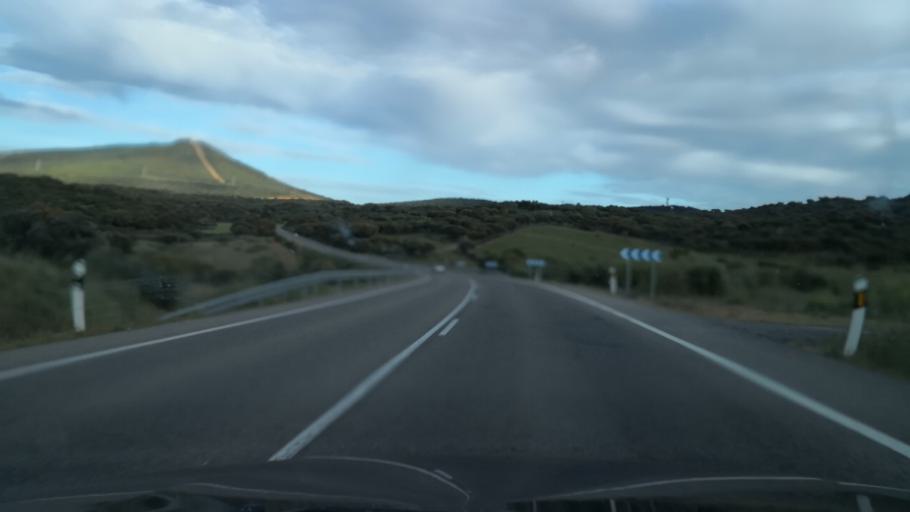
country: ES
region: Extremadura
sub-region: Provincia de Caceres
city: Pedroso de Acim
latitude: 39.8349
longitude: -6.3911
